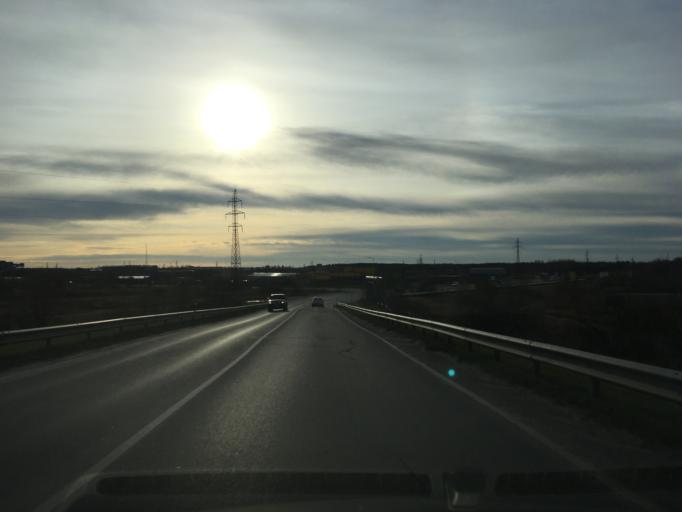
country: EE
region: Ida-Virumaa
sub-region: Narva linn
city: Narva
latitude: 59.3710
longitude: 28.1552
